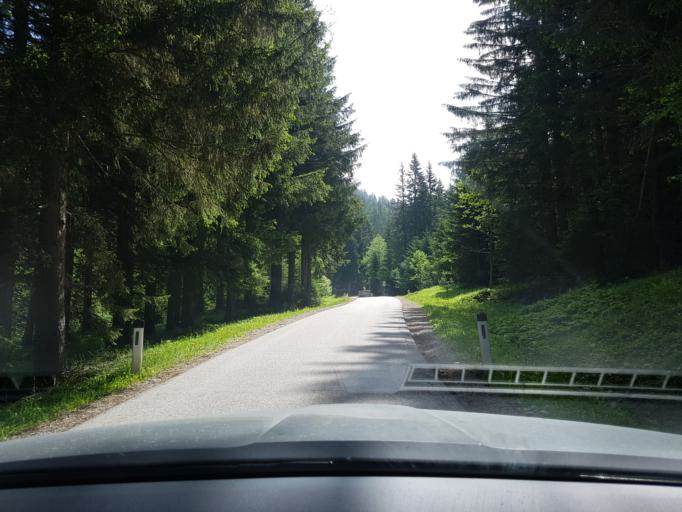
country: AT
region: Salzburg
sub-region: Politischer Bezirk Tamsweg
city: Thomatal
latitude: 47.0367
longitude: 13.7202
